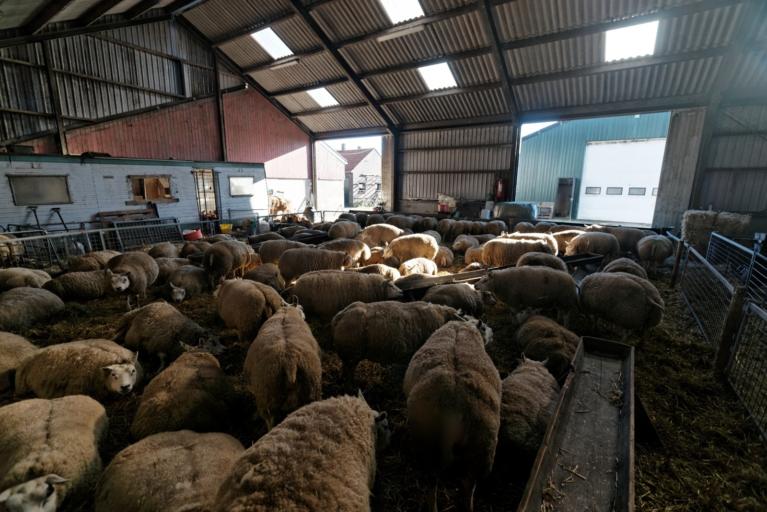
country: NL
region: North Holland
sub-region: Gemeente Texel
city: Den Burg
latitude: 53.0737
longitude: 4.8309
